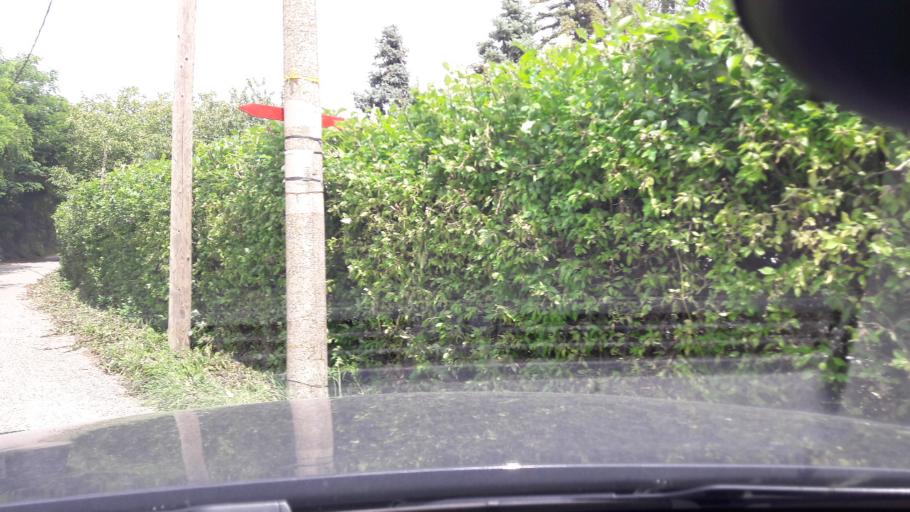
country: RS
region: Central Serbia
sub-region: Belgrade
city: Sopot
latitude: 44.6138
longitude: 20.5895
